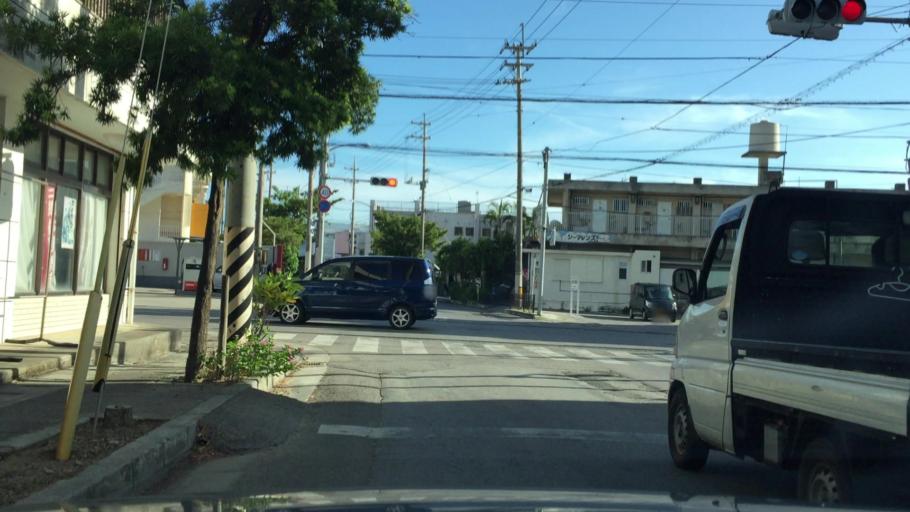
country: JP
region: Okinawa
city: Ishigaki
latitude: 24.3485
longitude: 124.1580
